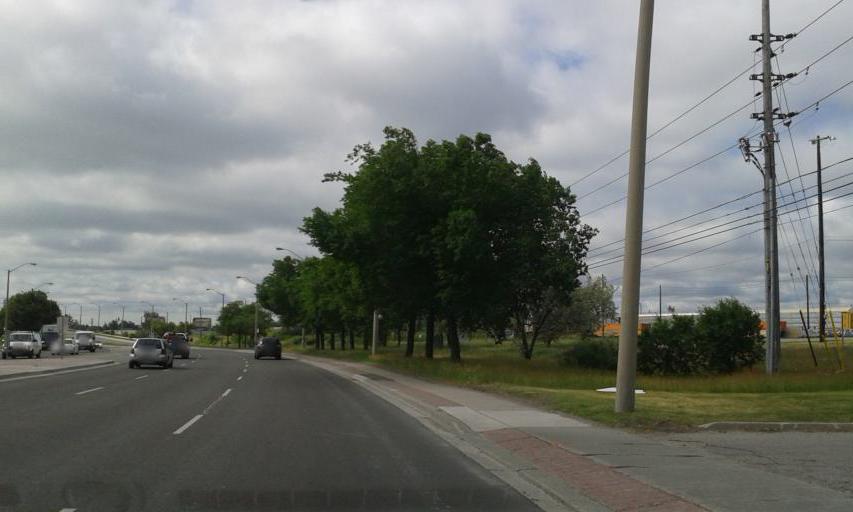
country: CA
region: Ontario
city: Scarborough
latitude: 43.8077
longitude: -79.2441
